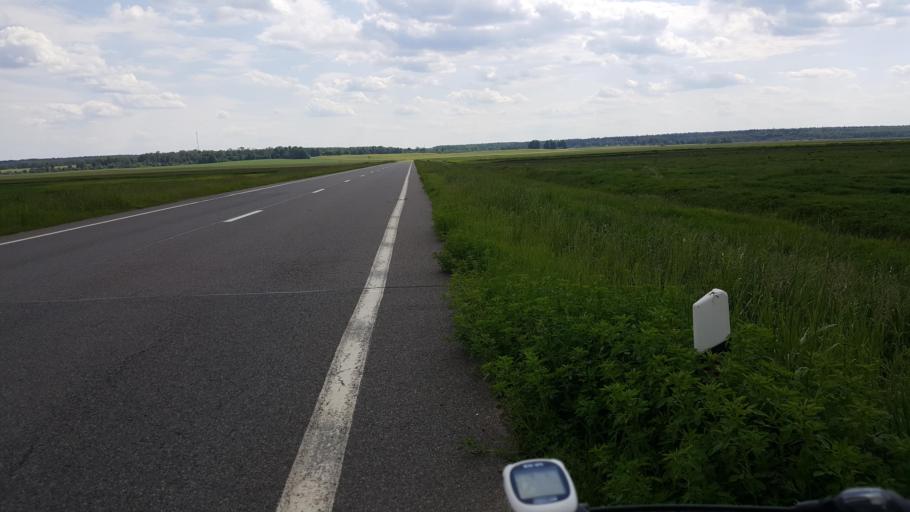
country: PL
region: Podlasie
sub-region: Powiat hajnowski
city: Bialowieza
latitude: 52.6414
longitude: 24.0778
